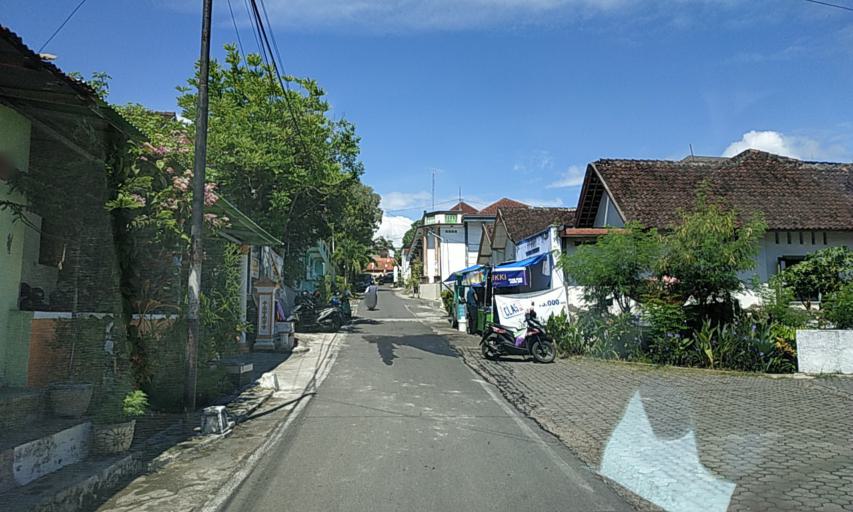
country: ID
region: Central Java
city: Selogiri
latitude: -7.8130
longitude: 110.9251
